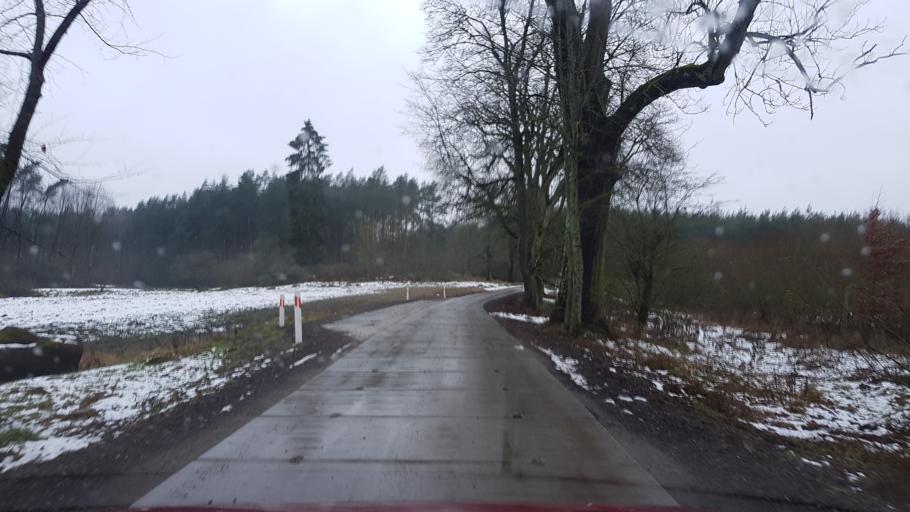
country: PL
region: West Pomeranian Voivodeship
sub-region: Powiat policki
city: Dobra
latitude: 53.5493
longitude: 14.4283
